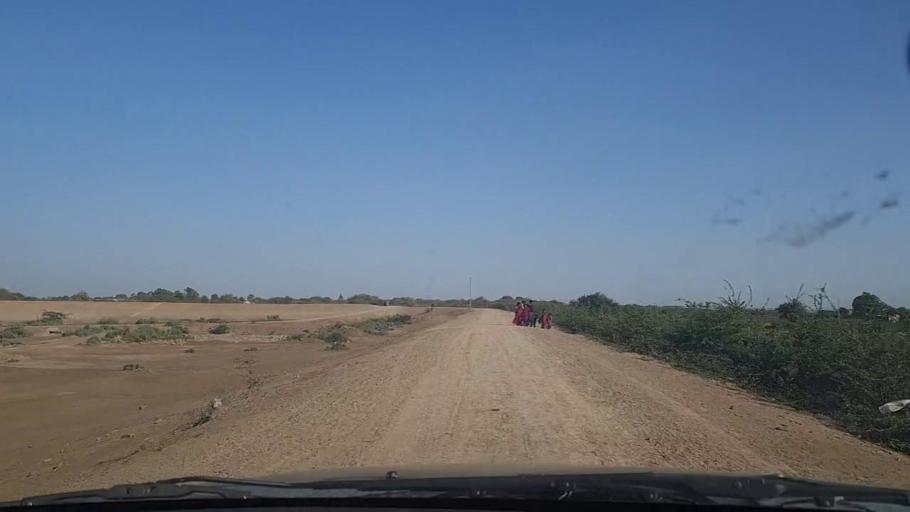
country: PK
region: Sindh
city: Chuhar Jamali
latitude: 24.3674
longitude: 67.7769
